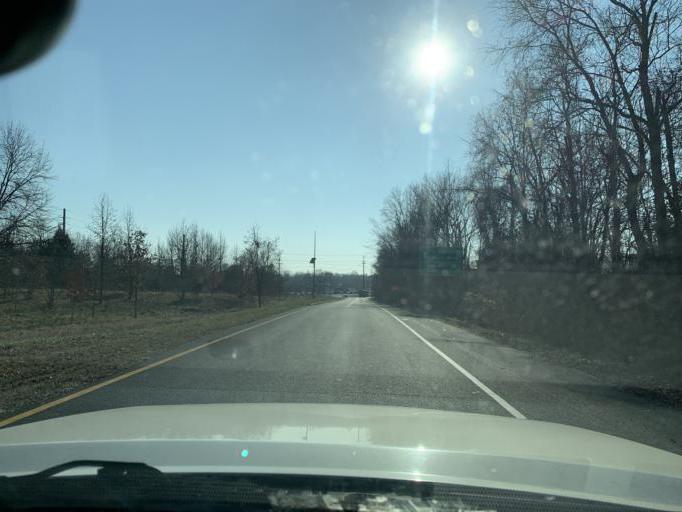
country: US
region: Maryland
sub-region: Prince George's County
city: Largo
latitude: 38.8939
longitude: -76.8488
